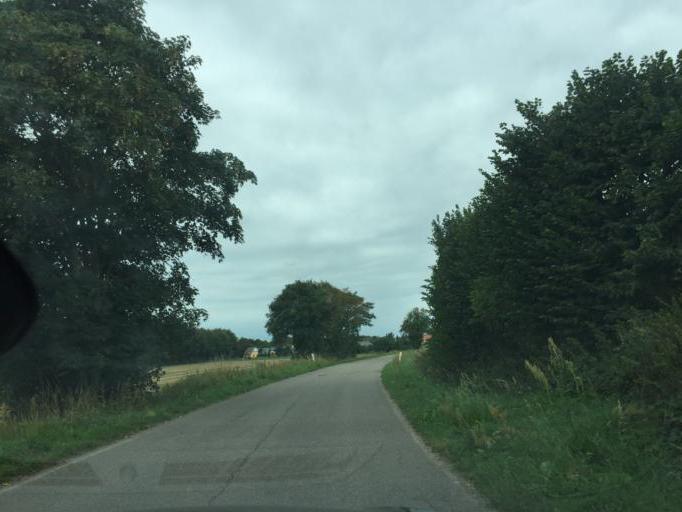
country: DK
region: South Denmark
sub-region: Assens Kommune
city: Vissenbjerg
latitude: 55.3735
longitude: 10.1105
